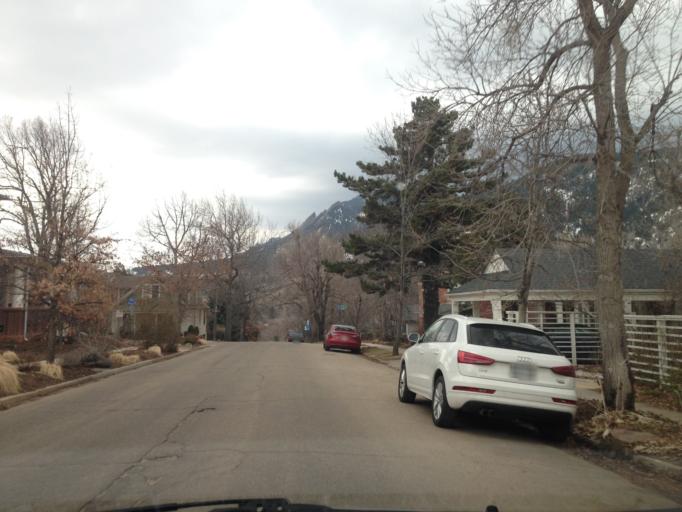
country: US
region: Colorado
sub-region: Boulder County
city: Boulder
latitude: 40.0190
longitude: -105.2916
